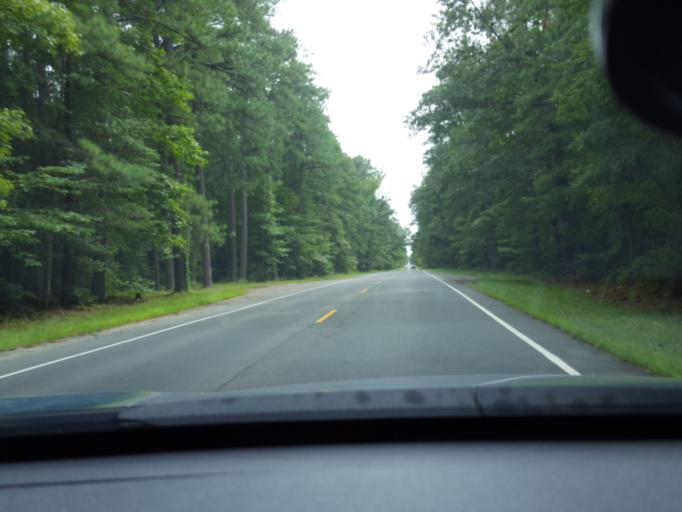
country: US
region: Virginia
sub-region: Caroline County
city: Bowling Green
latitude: 37.9755
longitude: -77.3404
